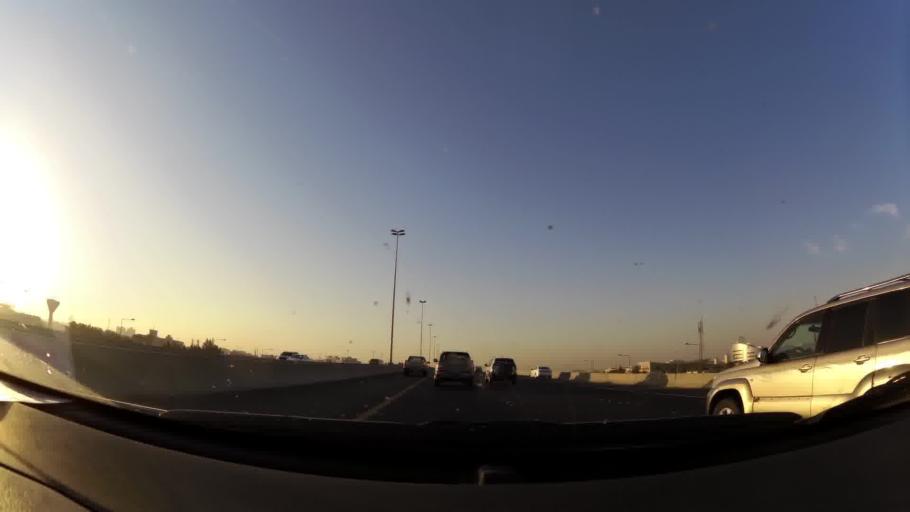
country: KW
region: Al Ahmadi
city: Al Manqaf
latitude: 29.0933
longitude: 48.1158
